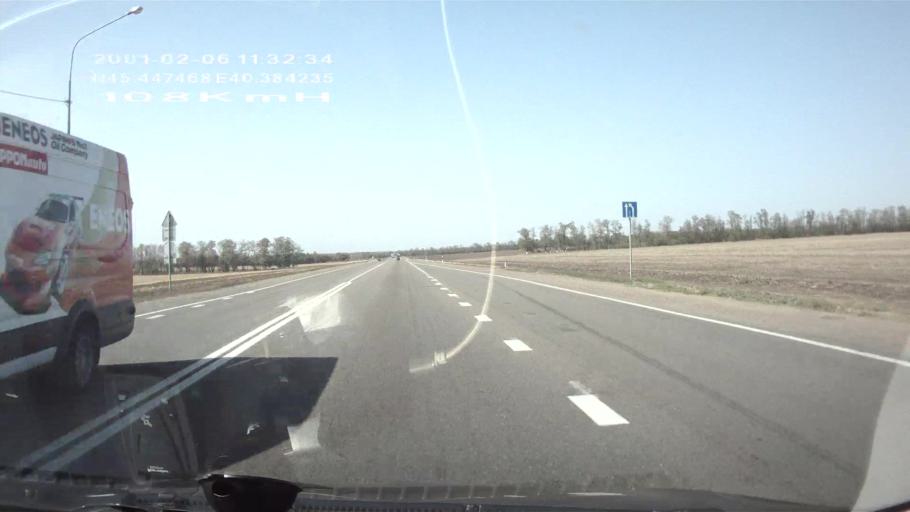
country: RU
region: Krasnodarskiy
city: Kazanskaya
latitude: 45.4470
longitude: 40.3827
